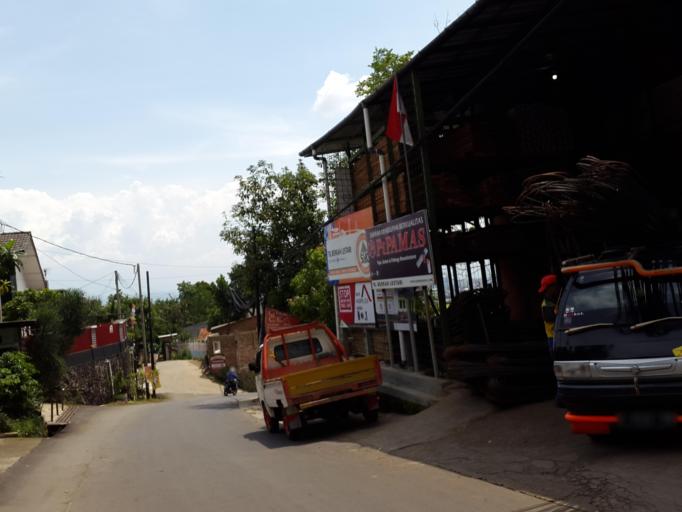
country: ID
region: West Java
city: Bandung
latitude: -6.8904
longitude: 107.6638
